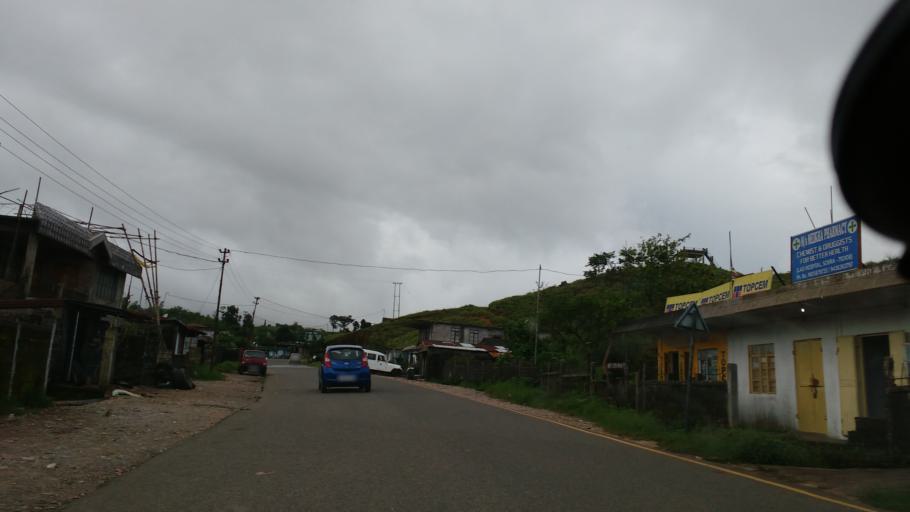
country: IN
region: Meghalaya
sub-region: East Khasi Hills
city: Cherrapunji
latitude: 25.2729
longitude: 91.7327
